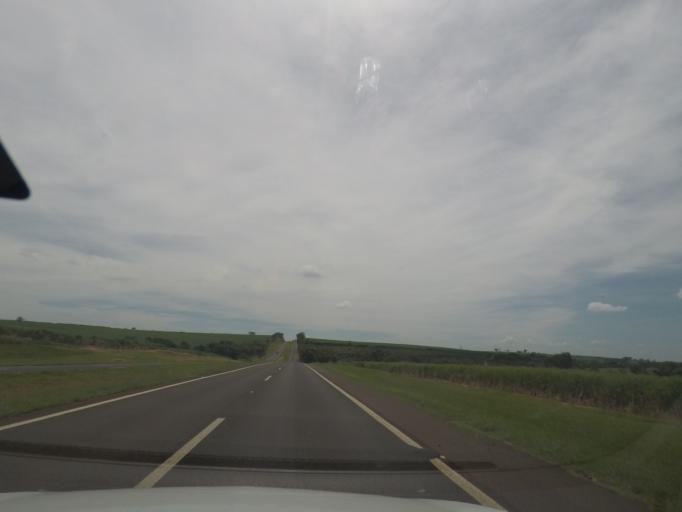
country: BR
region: Sao Paulo
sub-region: Bebedouro
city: Bebedouro
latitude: -21.0320
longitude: -48.4202
